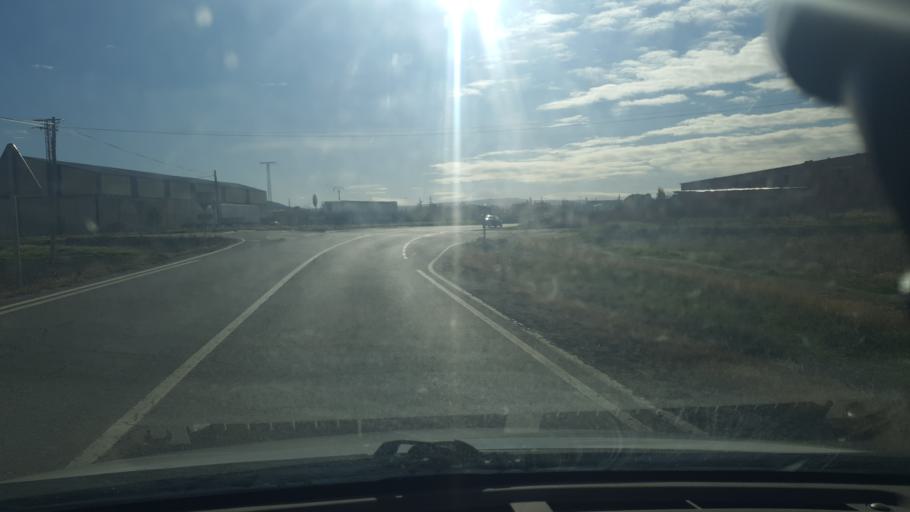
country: ES
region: Castille and Leon
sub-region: Provincia de Avila
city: Gotarrendura
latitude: 40.8033
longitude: -4.7591
